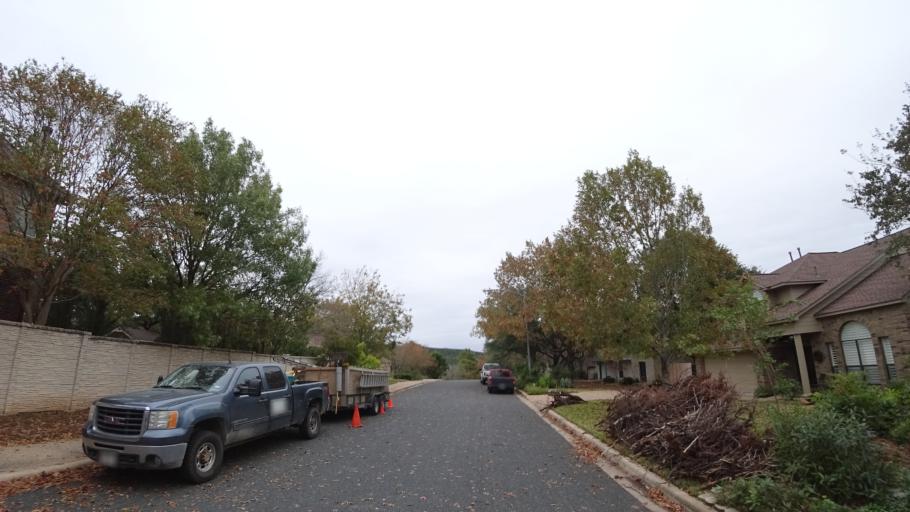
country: US
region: Texas
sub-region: Williamson County
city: Jollyville
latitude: 30.3805
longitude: -97.7896
